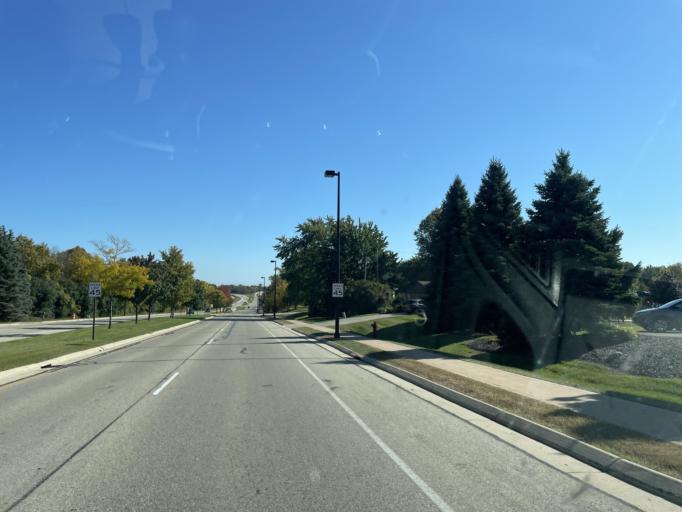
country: US
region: Wisconsin
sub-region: Waukesha County
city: Butler
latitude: 43.1438
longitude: -88.0682
